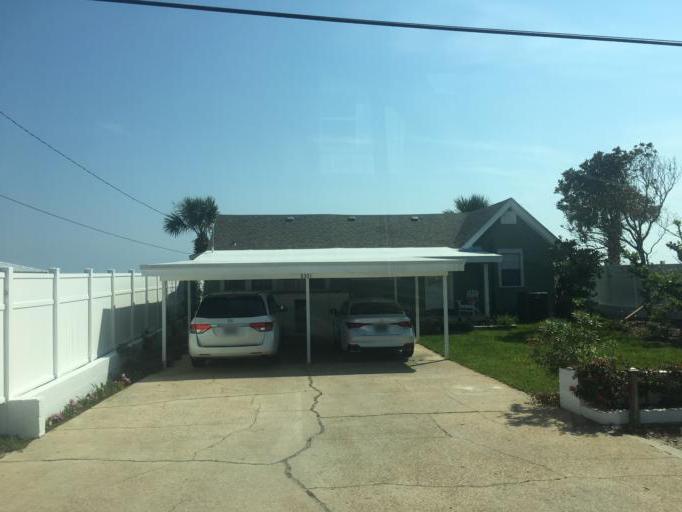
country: US
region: Florida
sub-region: Bay County
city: Panama City Beach
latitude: 30.1634
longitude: -85.7849
